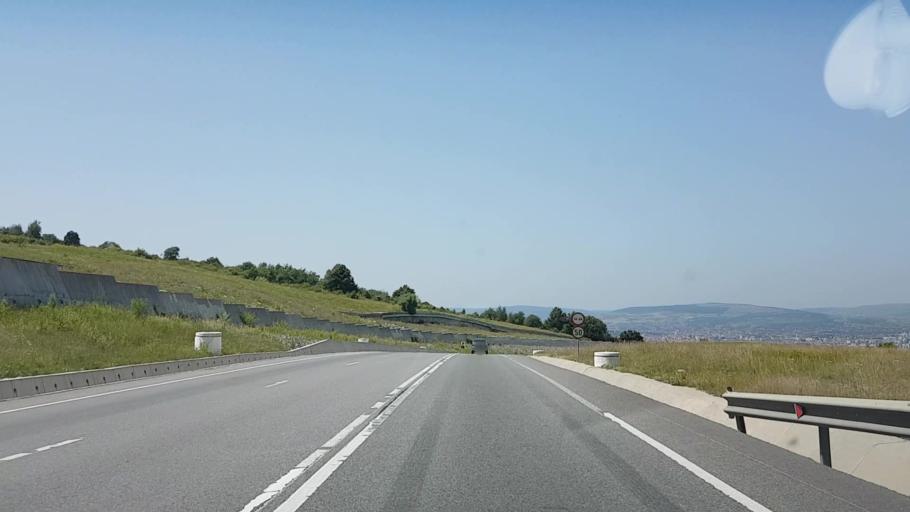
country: RO
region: Cluj
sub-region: Comuna Feleacu
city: Feleacu
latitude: 46.7217
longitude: 23.6483
